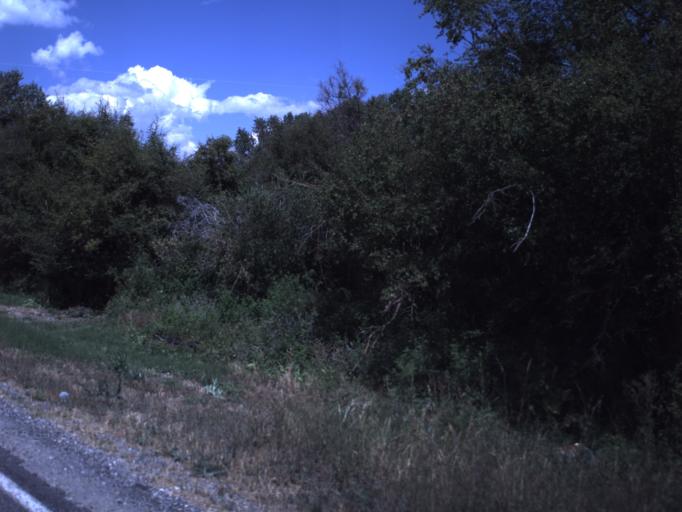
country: US
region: Idaho
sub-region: Bear Lake County
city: Paris
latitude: 41.9229
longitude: -111.3965
